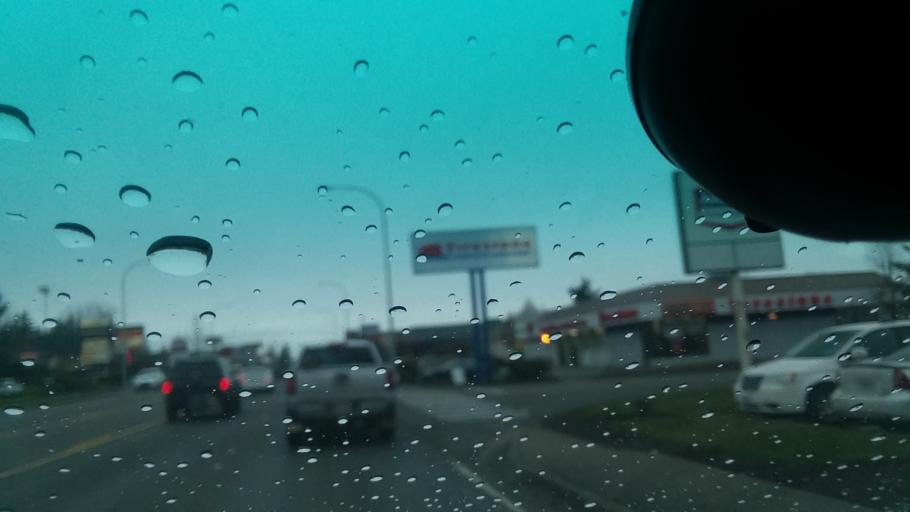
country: US
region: Washington
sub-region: Pierce County
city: South Hill
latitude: 47.1453
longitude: -122.2929
